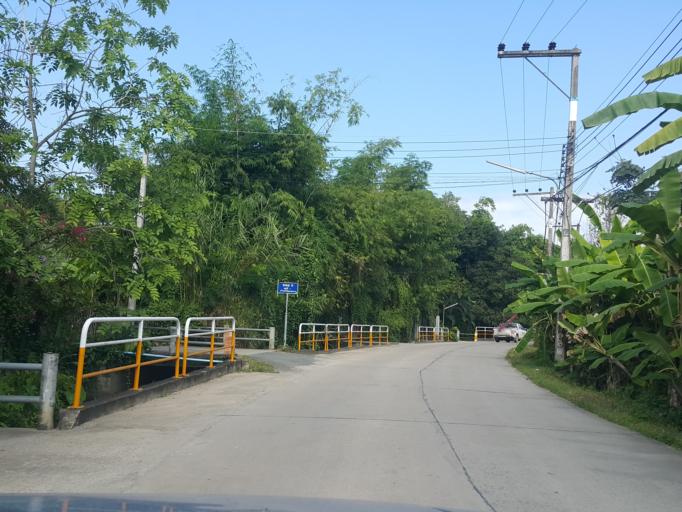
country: TH
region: Chiang Mai
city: Saraphi
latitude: 18.7296
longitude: 99.0427
